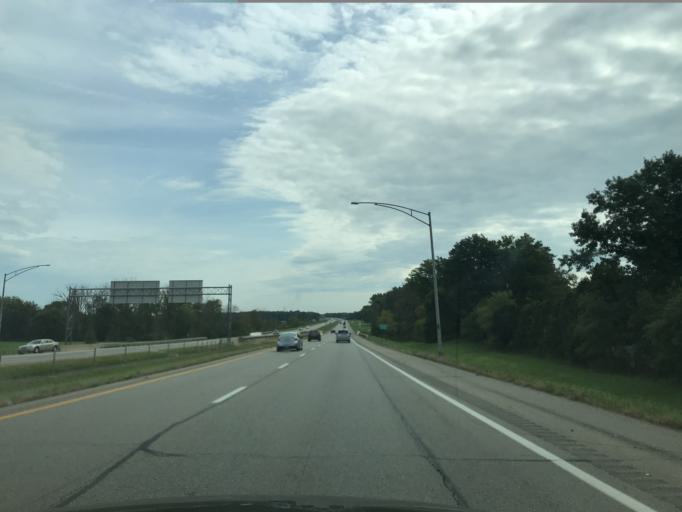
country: US
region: Ohio
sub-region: Trumbull County
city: Champion Heights
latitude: 41.2757
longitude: -80.8395
